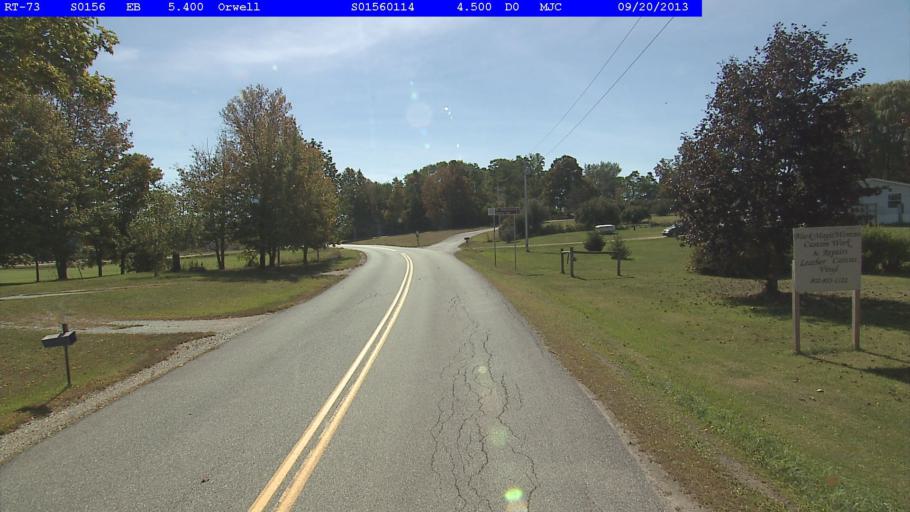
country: US
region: New York
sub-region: Essex County
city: Ticonderoga
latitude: 43.8056
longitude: -73.3123
